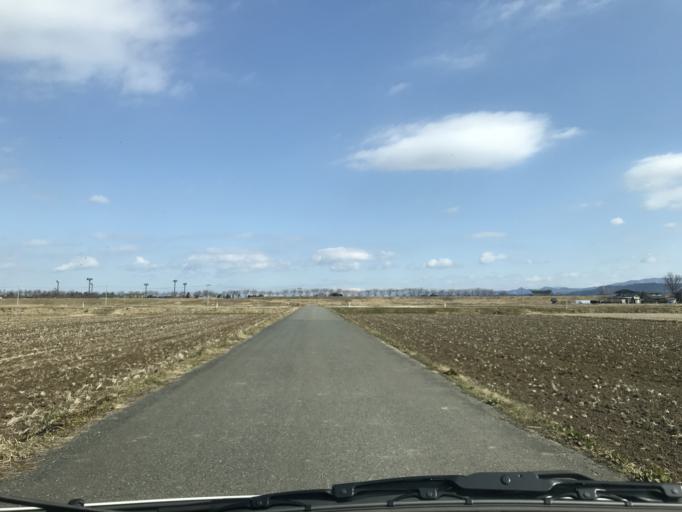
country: JP
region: Iwate
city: Mizusawa
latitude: 39.0499
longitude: 141.1408
